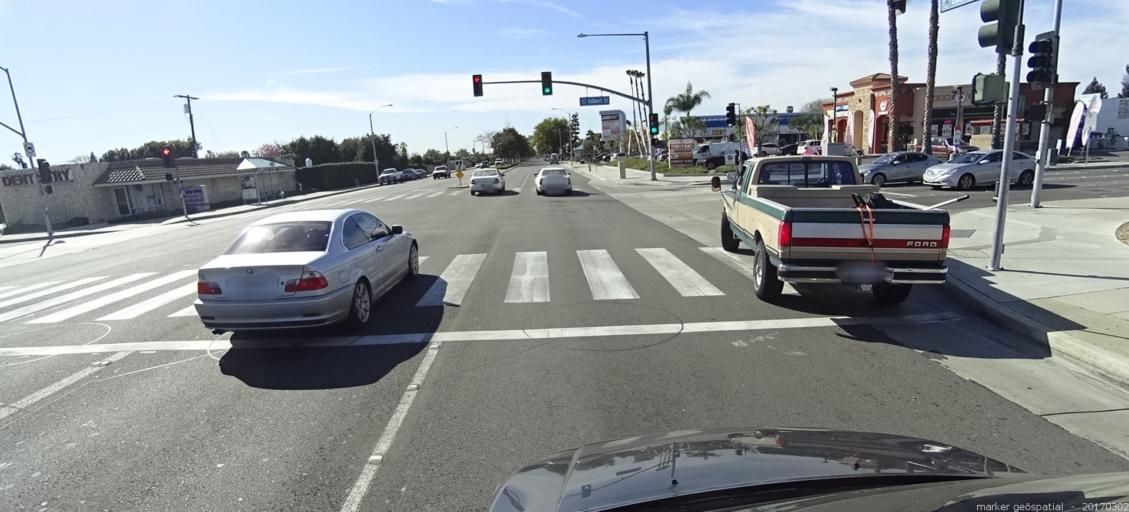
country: US
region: California
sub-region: Orange County
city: Stanton
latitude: 33.8324
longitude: -117.9674
